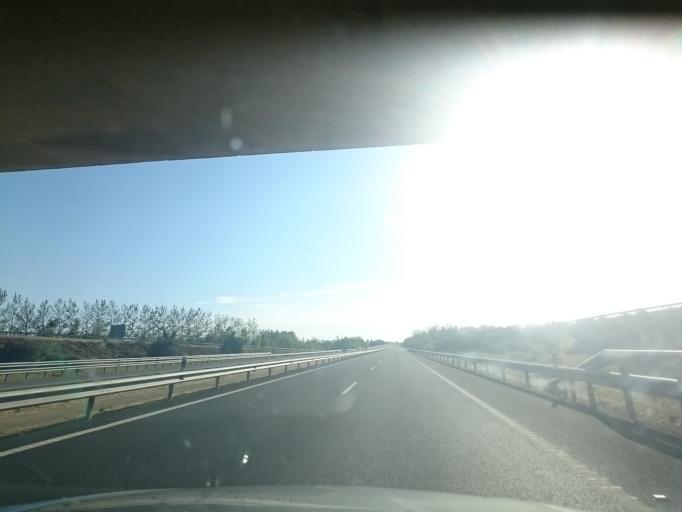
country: ES
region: Castille and Leon
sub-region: Provincia de Burgos
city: Sasamon
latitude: 42.3954
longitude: -4.0726
